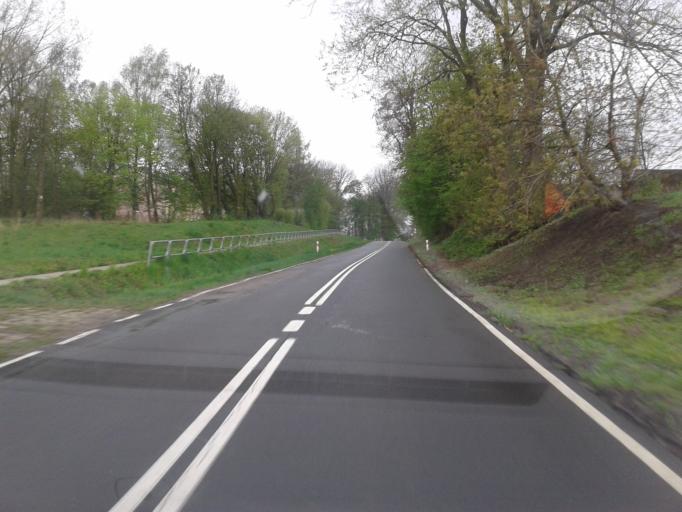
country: PL
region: Lublin Voivodeship
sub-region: Powiat tomaszowski
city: Telatyn
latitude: 50.5557
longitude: 23.9366
